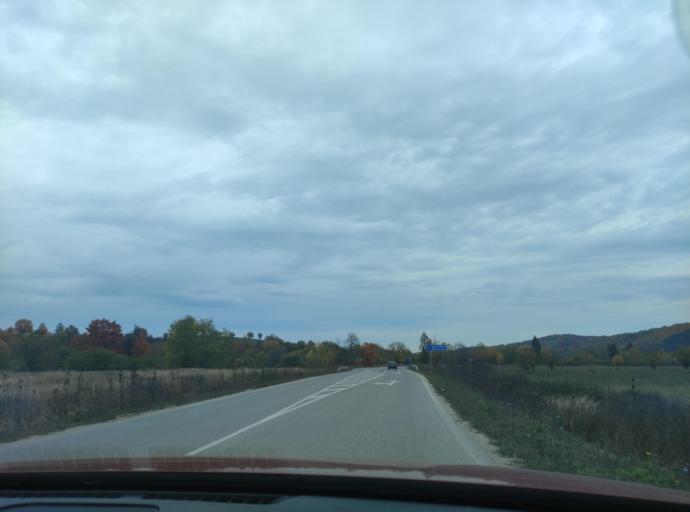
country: BG
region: Montana
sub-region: Obshtina Berkovitsa
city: Berkovitsa
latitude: 43.2510
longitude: 23.1683
